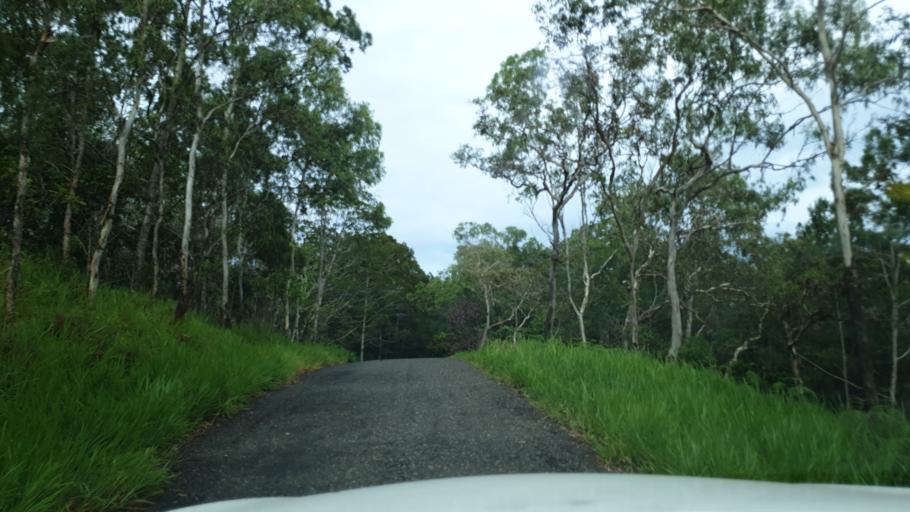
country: PG
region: National Capital
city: Port Moresby
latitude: -9.4350
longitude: 147.3746
